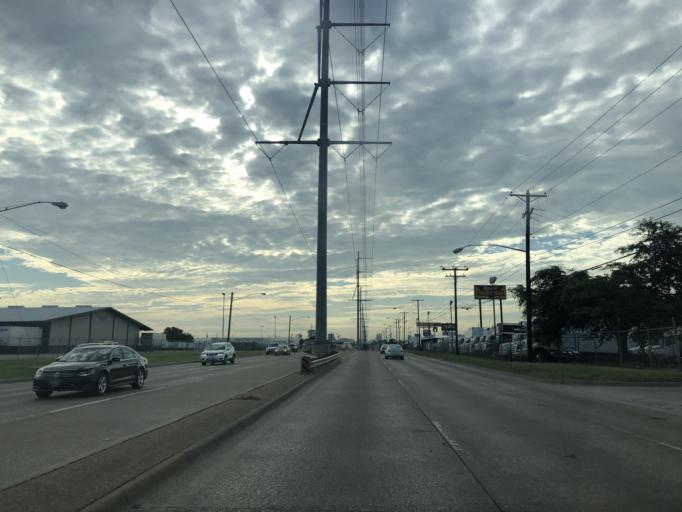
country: US
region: Texas
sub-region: Dallas County
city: Irving
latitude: 32.8081
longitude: -96.8894
